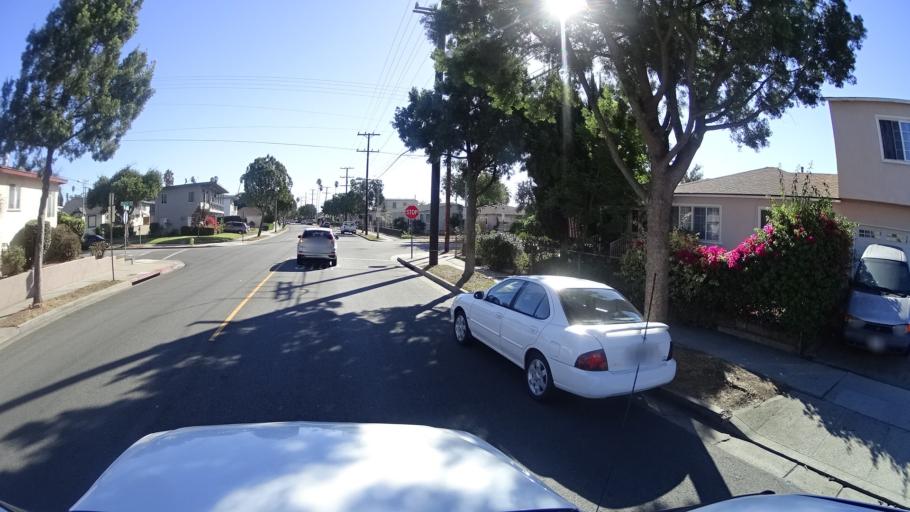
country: US
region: California
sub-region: Los Angeles County
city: Alhambra
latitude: 34.0875
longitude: -118.1400
